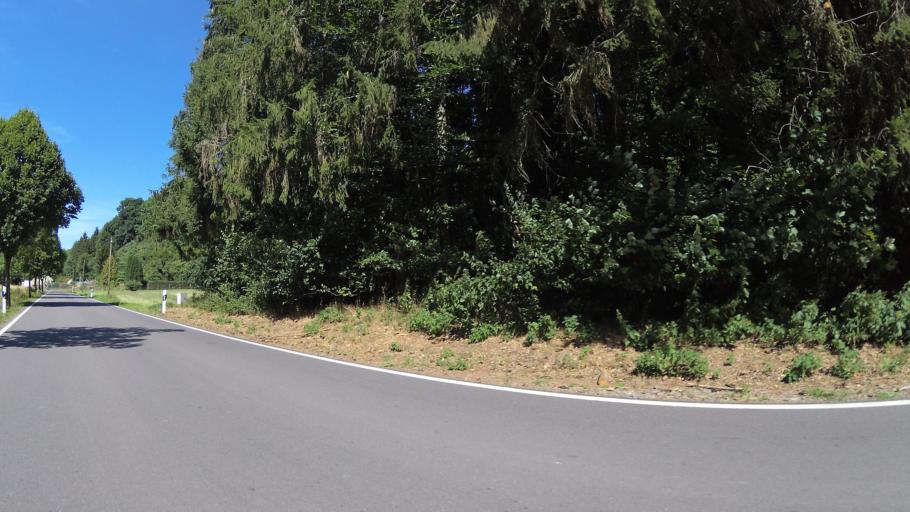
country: DE
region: Rheinland-Pfalz
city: Zweibrucken
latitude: 49.2404
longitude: 7.3161
